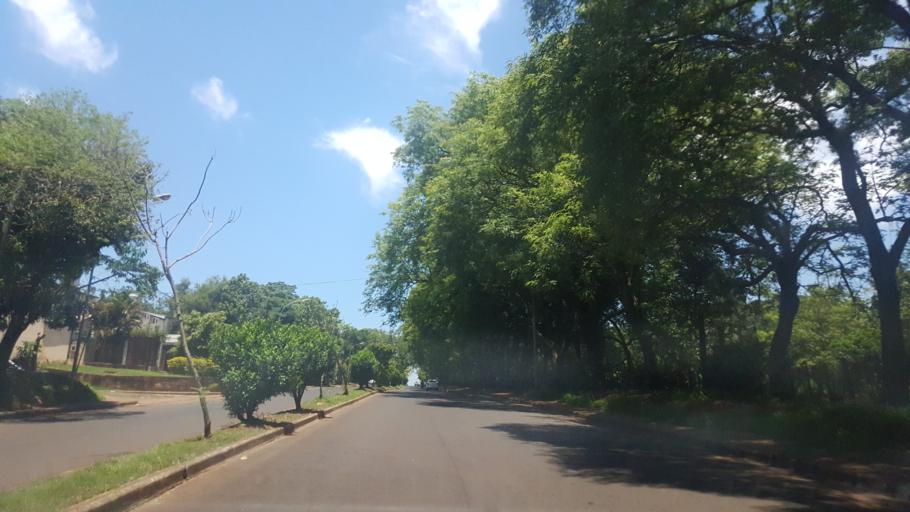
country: AR
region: Misiones
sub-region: Departamento de Capital
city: Posadas
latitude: -27.3570
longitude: -55.9379
